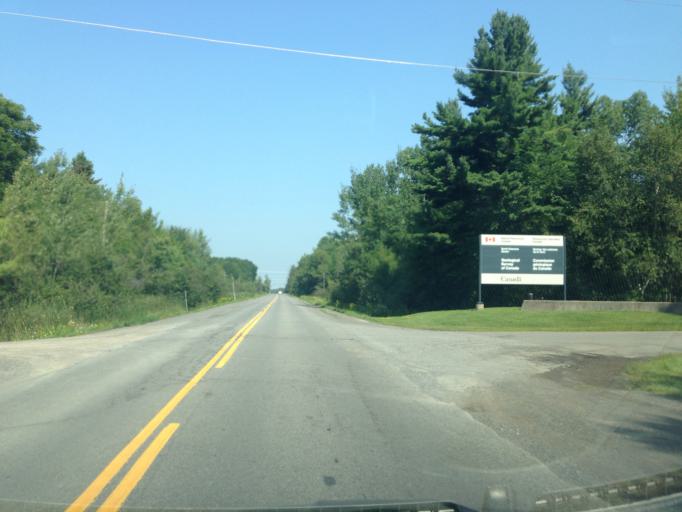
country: CA
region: Ontario
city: Ottawa
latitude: 45.4046
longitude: -75.5586
